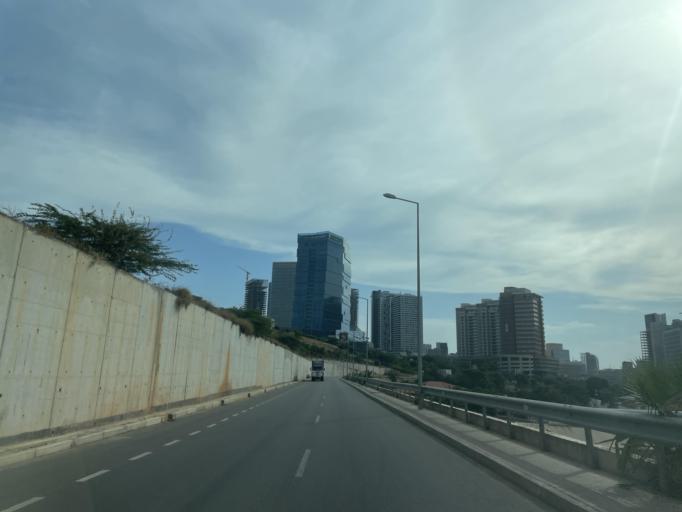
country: AO
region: Luanda
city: Luanda
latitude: -8.8082
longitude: 13.2451
